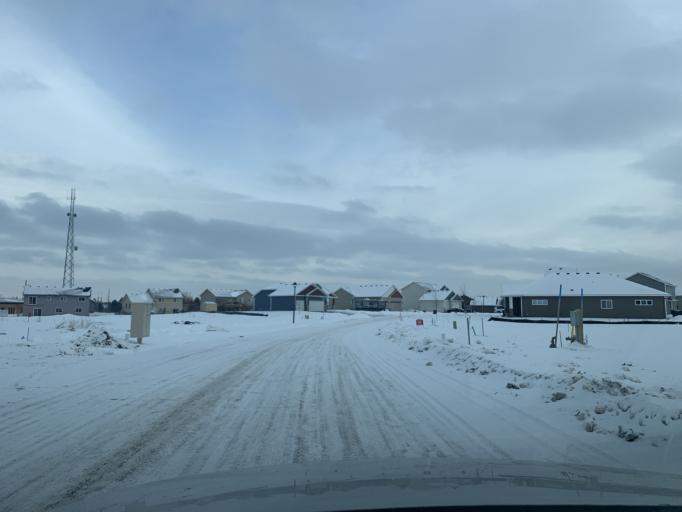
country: US
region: Minnesota
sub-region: Anoka County
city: Ramsey
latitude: 45.2466
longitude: -93.4127
